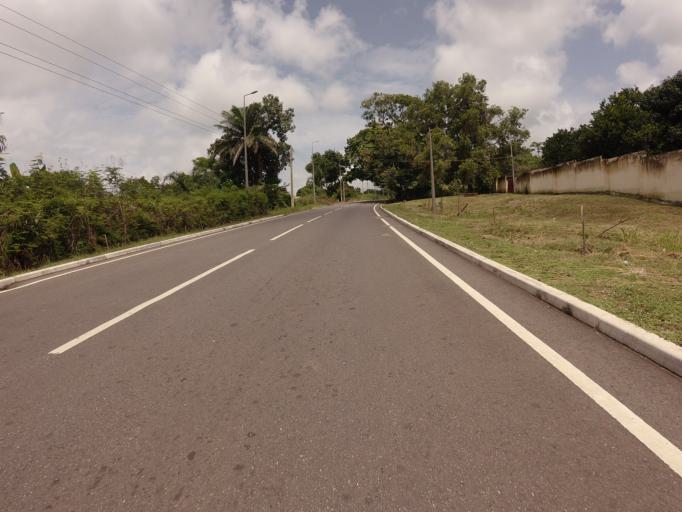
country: GH
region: Volta
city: Ho
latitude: 6.6077
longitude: 0.4639
